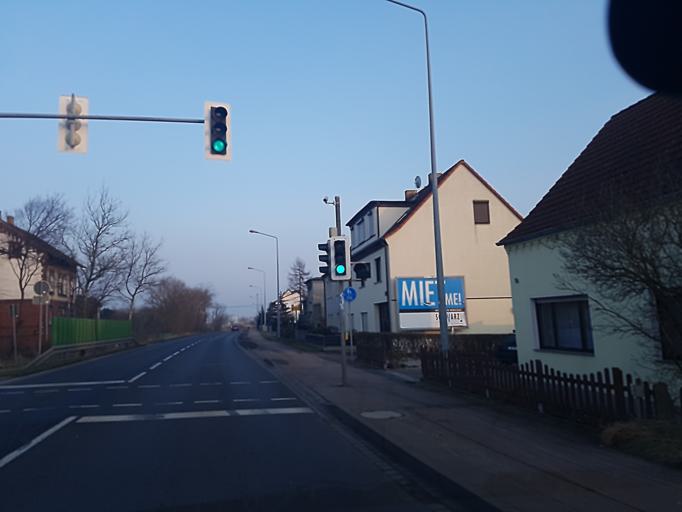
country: DE
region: Saxony-Anhalt
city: Nudersdorf
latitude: 51.8767
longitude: 12.5496
